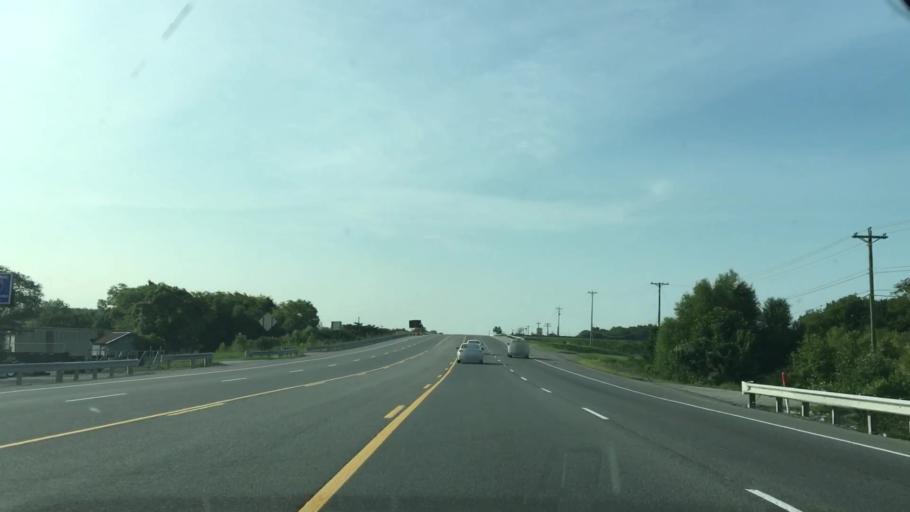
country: US
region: Tennessee
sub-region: Wilson County
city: Mount Juliet
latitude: 36.2299
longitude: -86.4279
